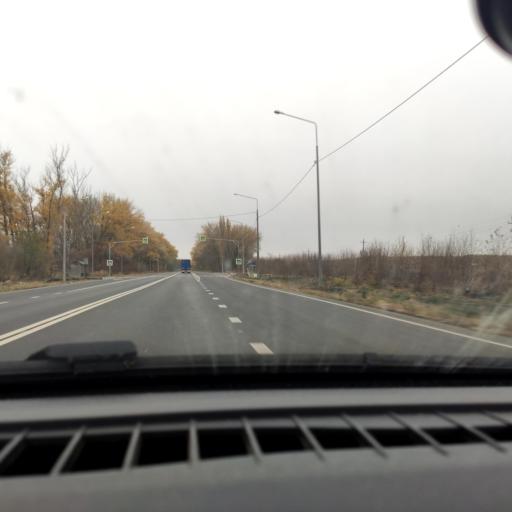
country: RU
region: Voronezj
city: Uryv-Pokrovka
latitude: 51.1727
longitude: 39.0764
